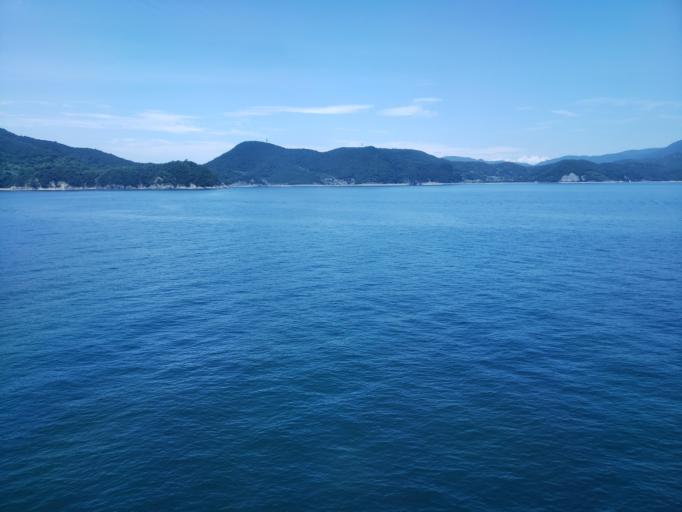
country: JP
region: Kagawa
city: Tonosho
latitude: 34.4169
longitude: 134.2607
